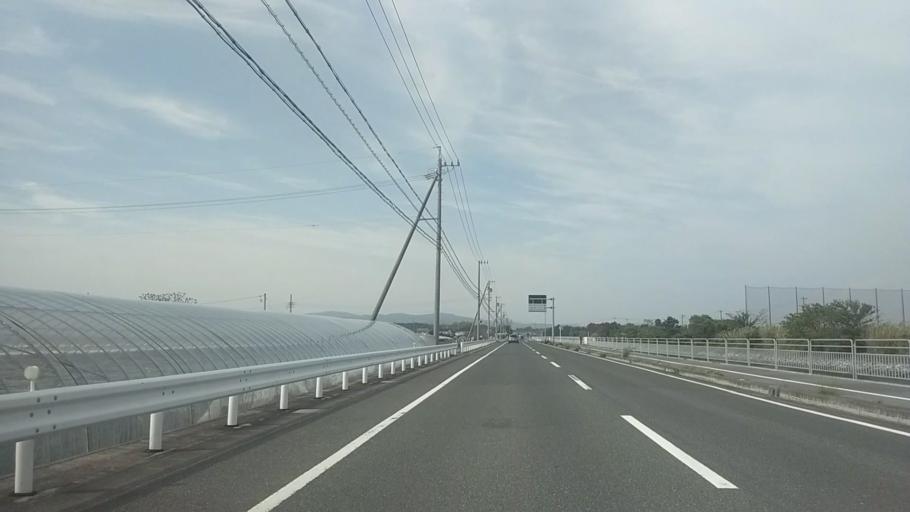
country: JP
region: Shizuoka
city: Kosai-shi
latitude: 34.7128
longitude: 137.5903
